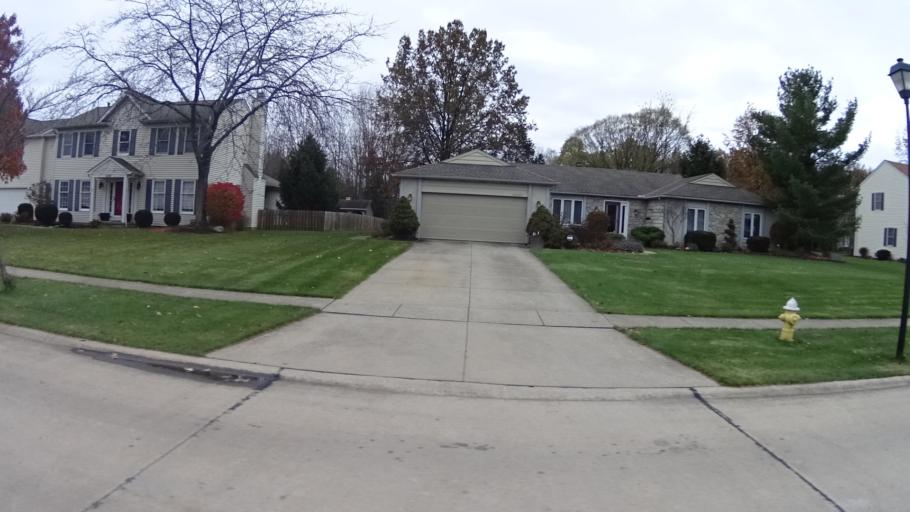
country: US
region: Ohio
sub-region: Lorain County
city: Avon Center
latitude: 41.4860
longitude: -81.9898
